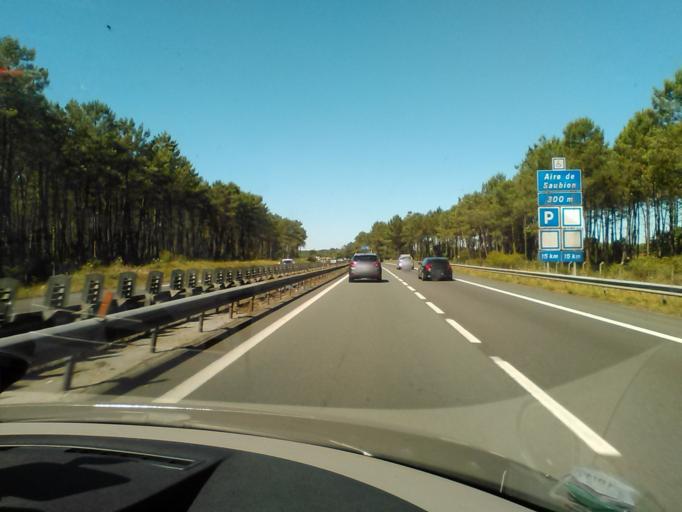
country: FR
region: Aquitaine
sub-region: Departement des Landes
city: Saint-Vincent-de-Tyrosse
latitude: 43.6807
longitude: -1.2962
